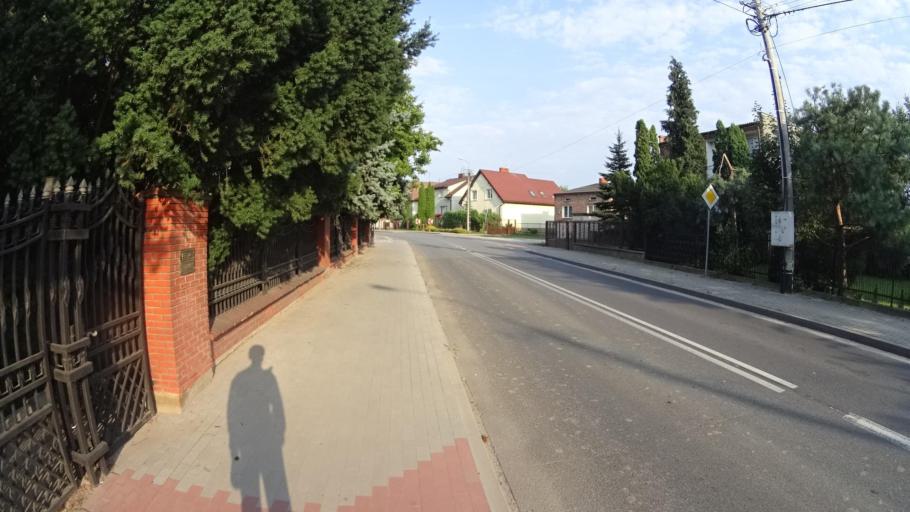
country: PL
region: Masovian Voivodeship
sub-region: Powiat pruszkowski
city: Rybie
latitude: 52.1455
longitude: 20.9499
